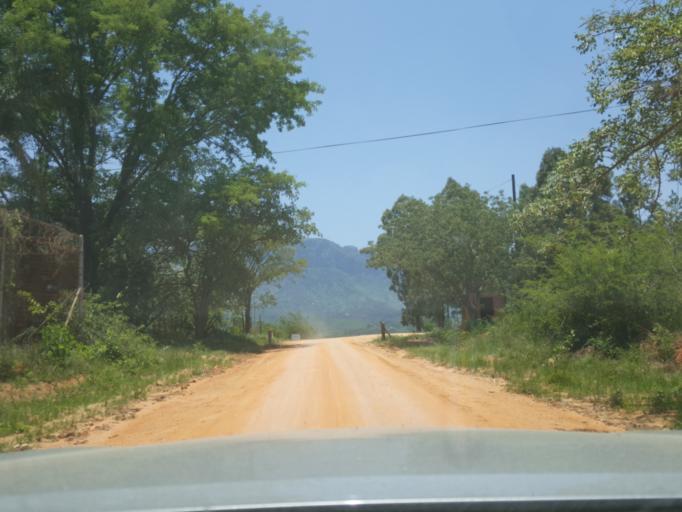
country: ZA
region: Limpopo
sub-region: Mopani District Municipality
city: Hoedspruit
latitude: -24.5923
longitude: 30.9407
